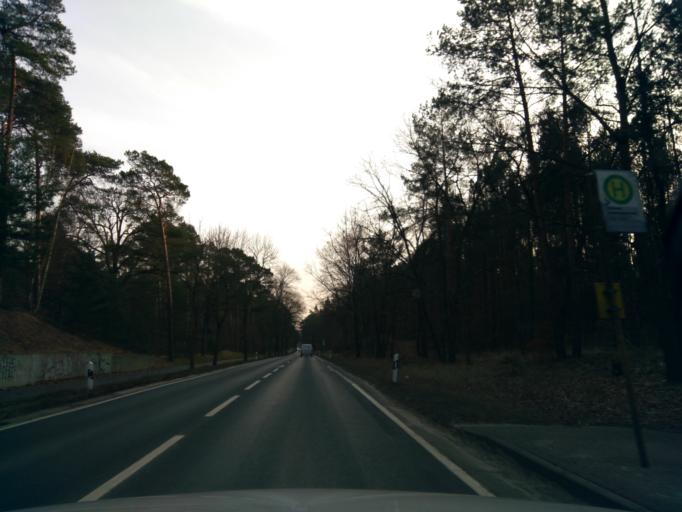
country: DE
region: Brandenburg
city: Falkensee
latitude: 52.5853
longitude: 13.0994
